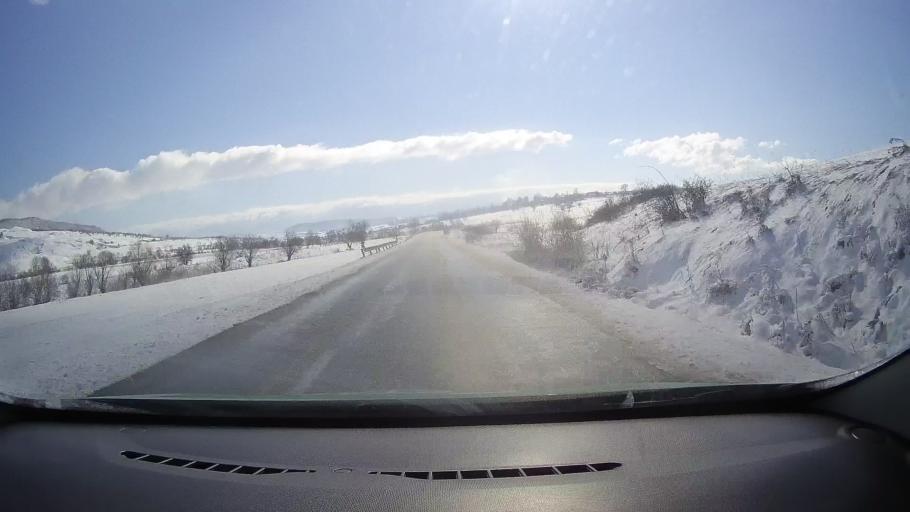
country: RO
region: Sibiu
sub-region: Comuna Rosia
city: Rosia
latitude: 45.8268
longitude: 24.3138
